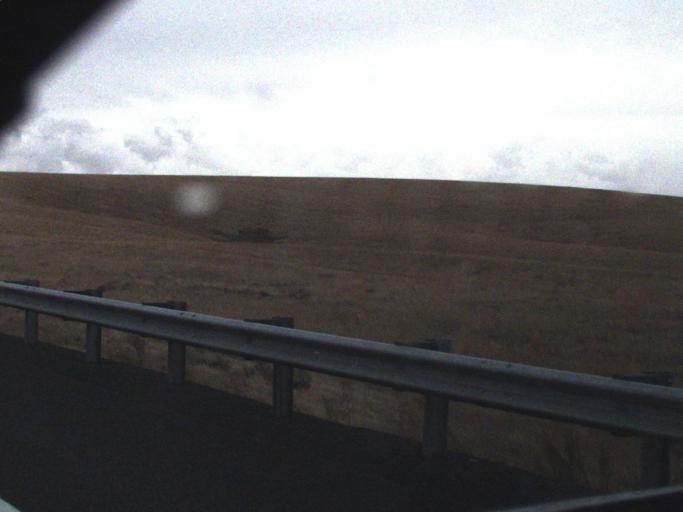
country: US
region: Washington
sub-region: Adams County
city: Ritzville
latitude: 46.7770
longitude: -118.3744
